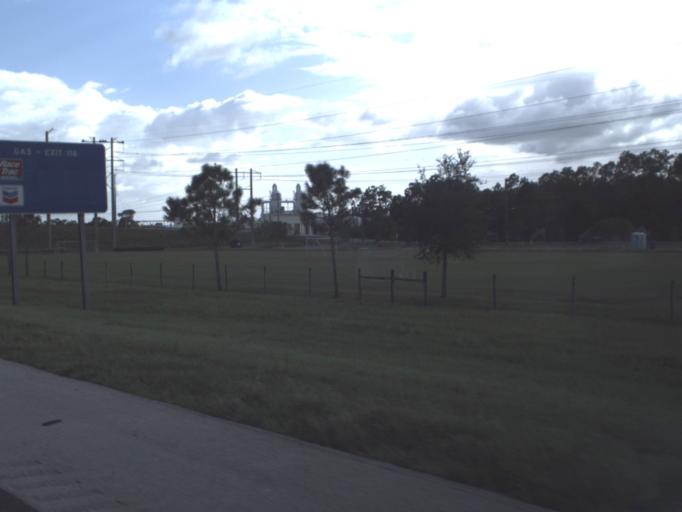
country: US
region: Florida
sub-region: Lee County
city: Bonita Springs
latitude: 26.3483
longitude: -81.7541
